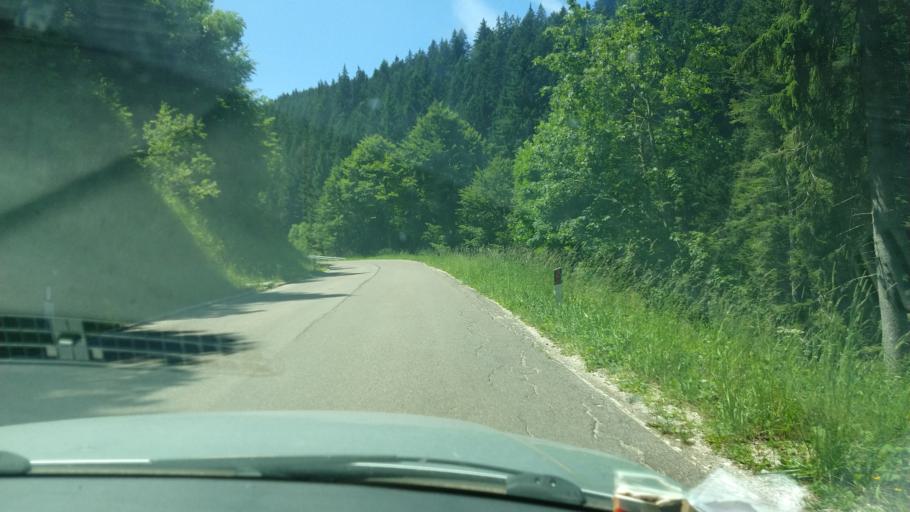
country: IT
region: Trentino-Alto Adige
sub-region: Provincia di Trento
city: Folgaria
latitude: 45.8997
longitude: 11.2103
